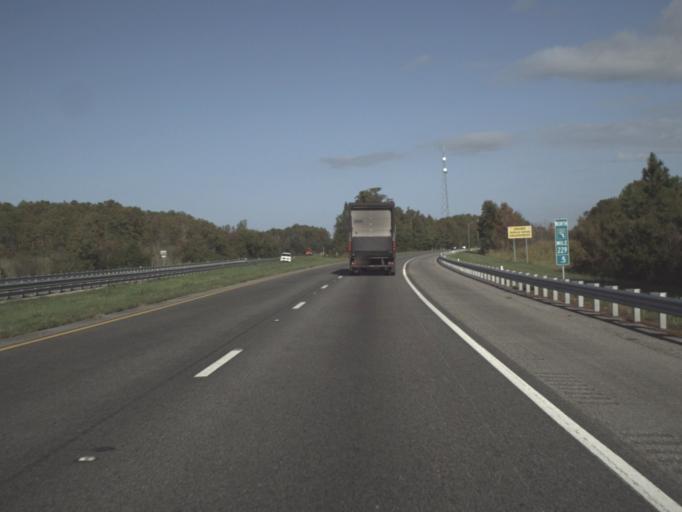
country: US
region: Florida
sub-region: Osceola County
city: Saint Cloud
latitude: 28.0873
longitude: -81.2666
